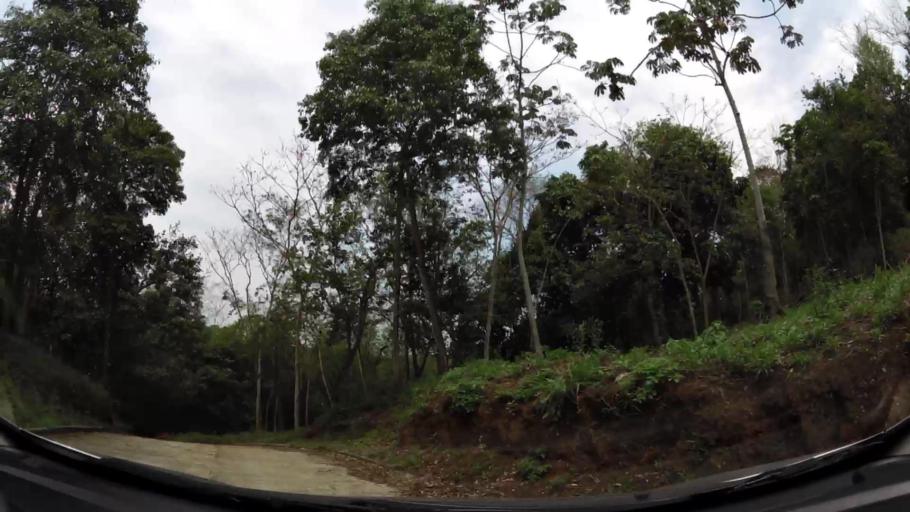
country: PY
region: Alto Parana
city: Ciudad del Este
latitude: -25.4884
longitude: -54.6055
